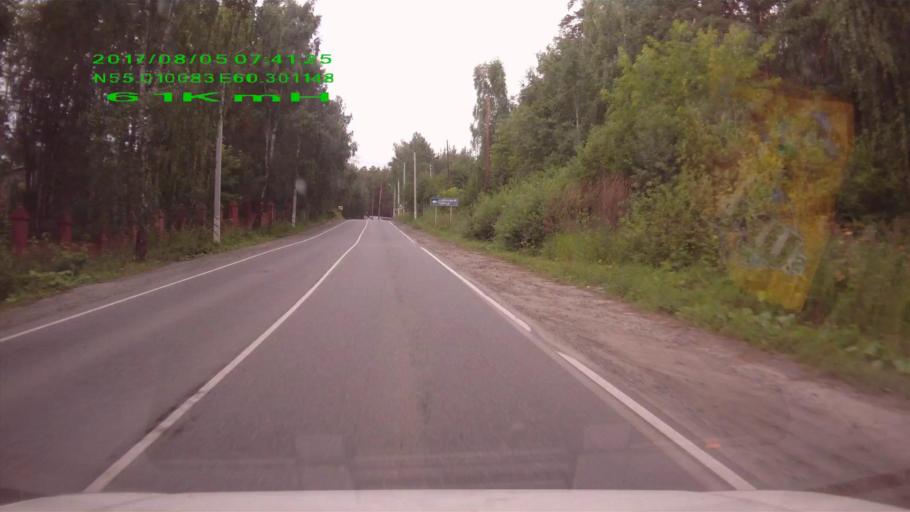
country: RU
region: Chelyabinsk
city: Chebarkul'
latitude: 55.0098
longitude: 60.3008
